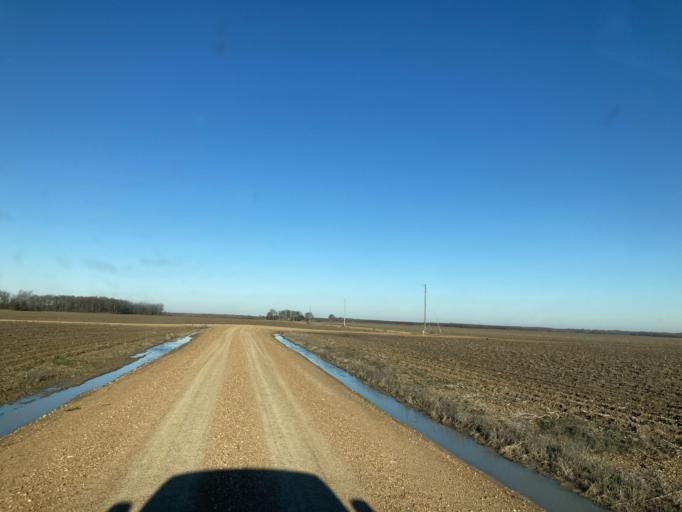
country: US
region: Mississippi
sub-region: Yazoo County
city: Yazoo City
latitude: 32.9246
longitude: -90.6126
